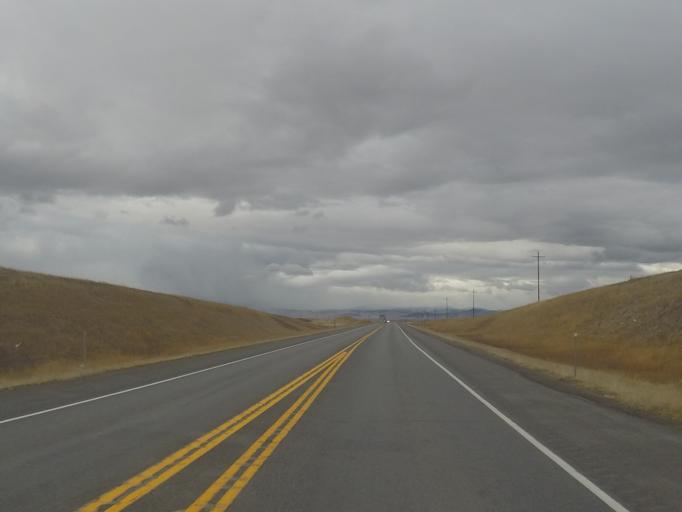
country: US
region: Montana
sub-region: Lewis and Clark County
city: East Helena
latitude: 46.5643
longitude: -111.7971
